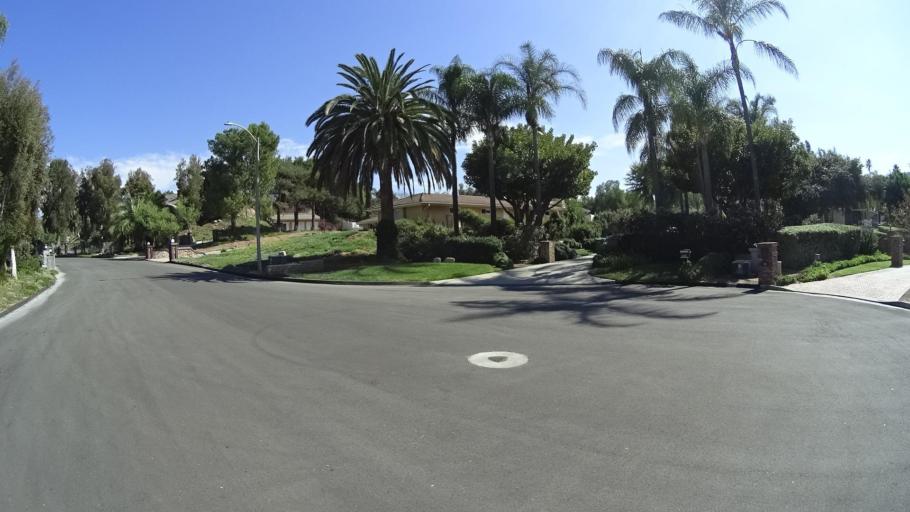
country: US
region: California
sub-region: San Diego County
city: Granite Hills
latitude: 32.7859
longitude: -116.9041
